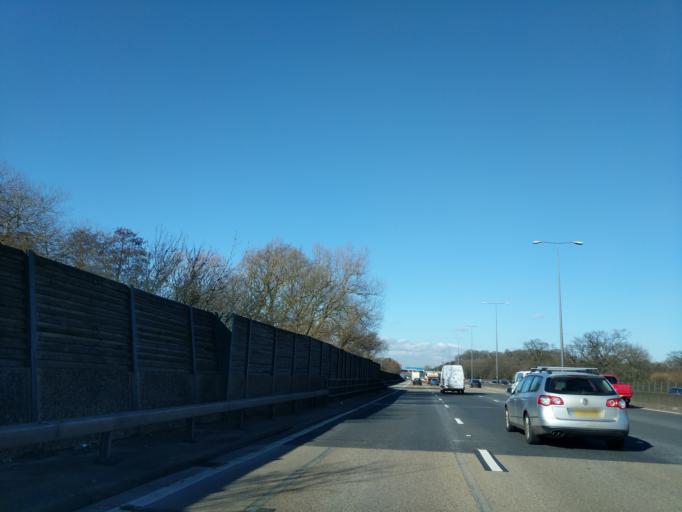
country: GB
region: England
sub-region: Surrey
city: Addlestone
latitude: 51.3578
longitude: -0.4950
